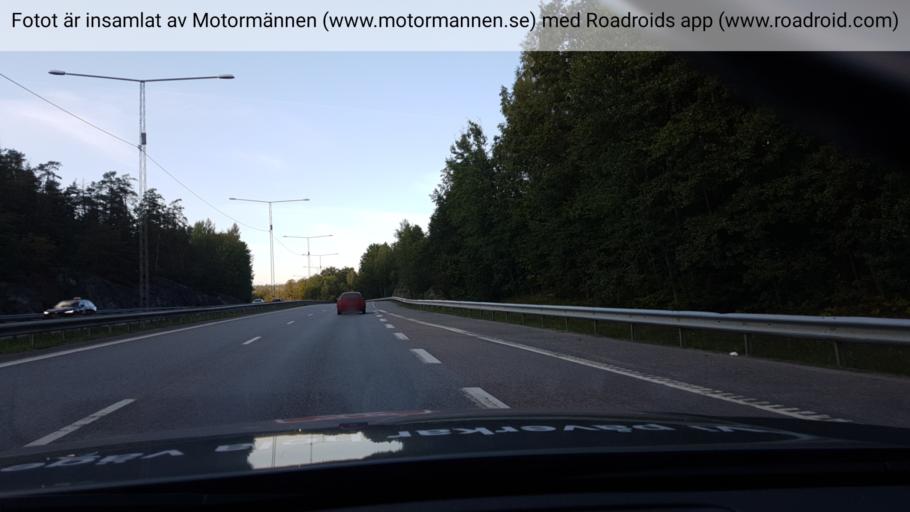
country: SE
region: Stockholm
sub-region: Nacka Kommun
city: Alta
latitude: 59.2525
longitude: 18.1704
